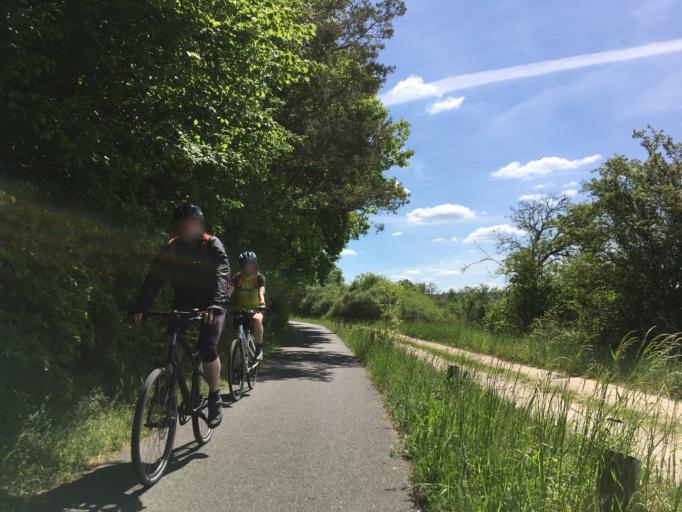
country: DE
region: Brandenburg
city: Niederfinow
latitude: 52.8469
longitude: 13.8893
